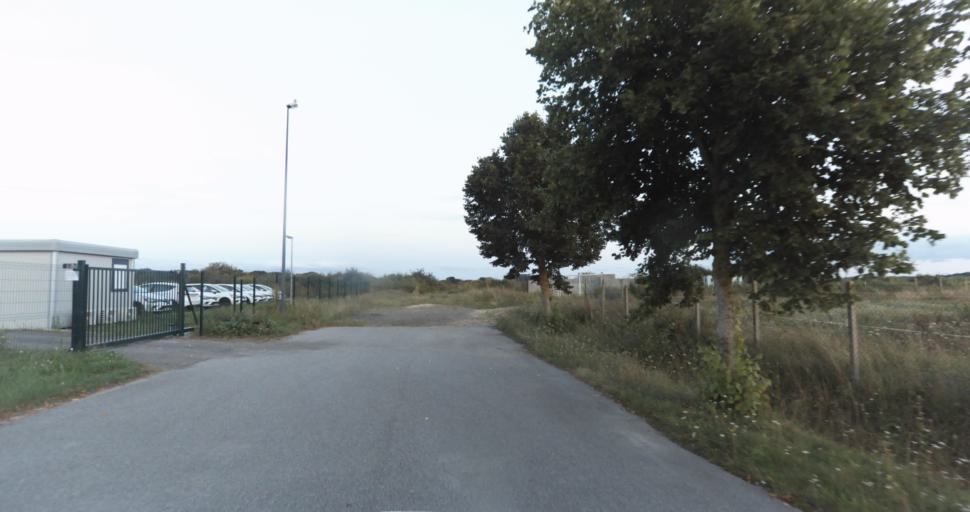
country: FR
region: Haute-Normandie
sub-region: Departement de l'Eure
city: Marcilly-sur-Eure
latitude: 48.8934
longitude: 1.2724
